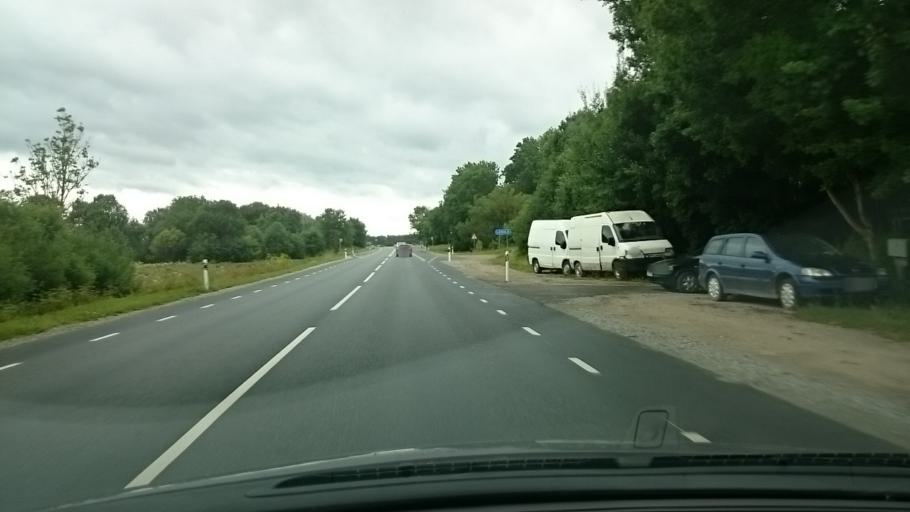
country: EE
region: Harju
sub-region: Keila linn
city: Keila
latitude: 59.2959
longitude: 24.3437
